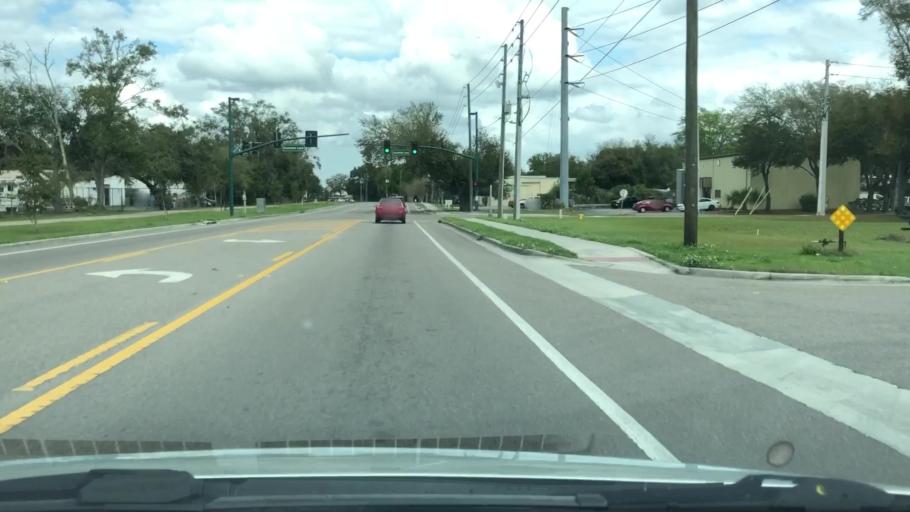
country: US
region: Florida
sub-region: Seminole County
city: Forest City
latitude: 28.6557
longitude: -81.4257
